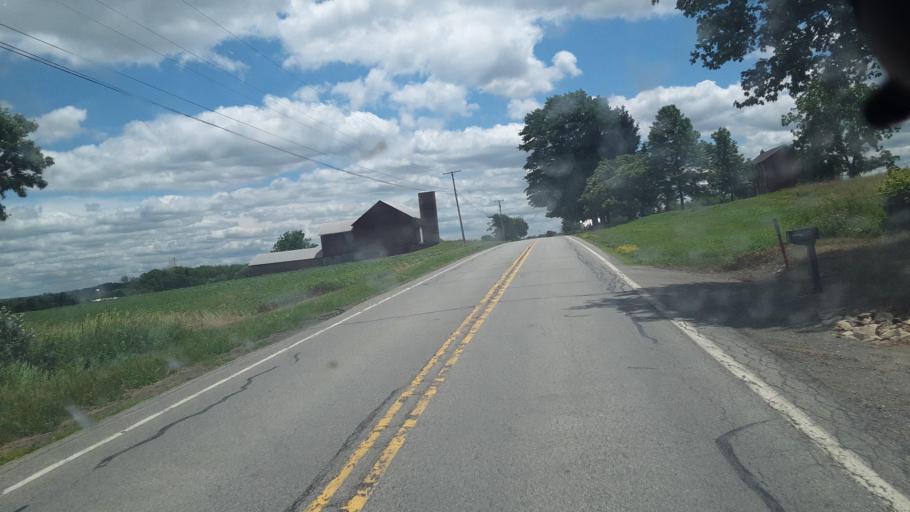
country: US
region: Pennsylvania
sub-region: Butler County
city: Slippery Rock
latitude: 41.0560
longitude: -80.2009
